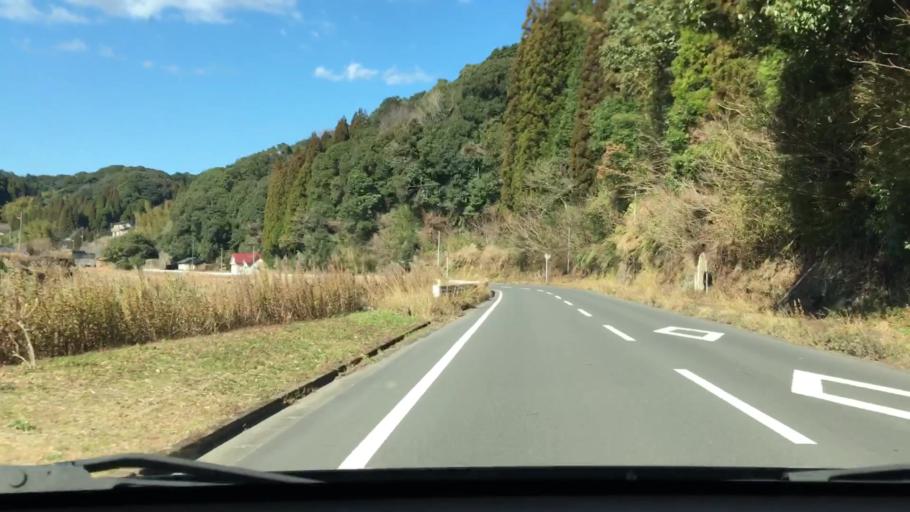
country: JP
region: Kagoshima
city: Ijuin
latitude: 31.6970
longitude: 130.4610
